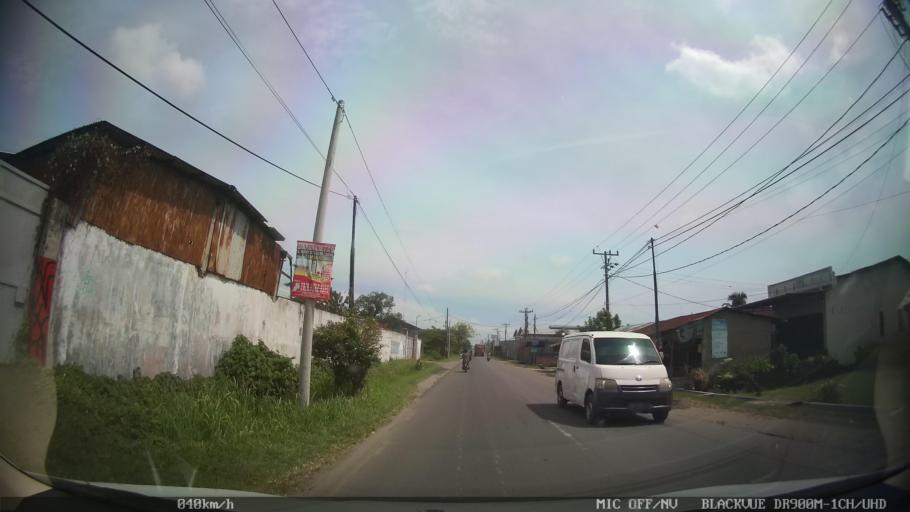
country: ID
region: North Sumatra
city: Medan
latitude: 3.6485
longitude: 98.7169
